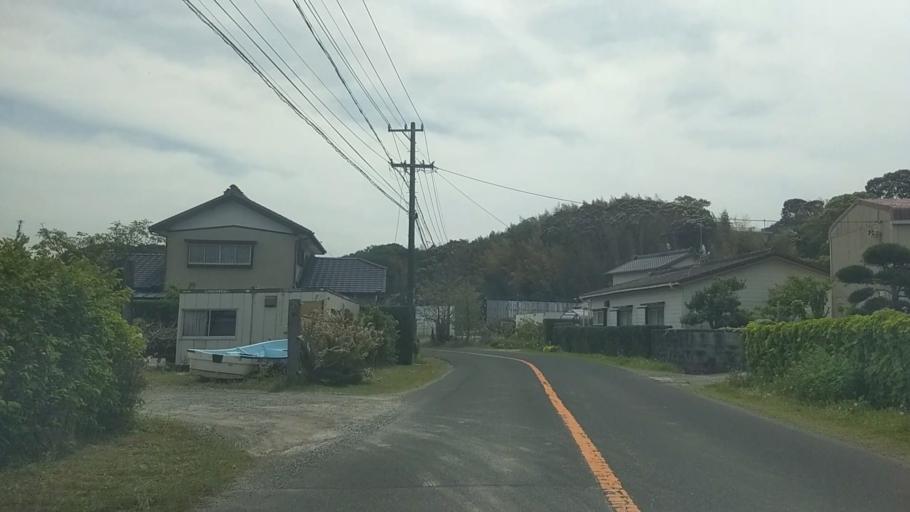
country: JP
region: Shizuoka
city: Kosai-shi
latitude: 34.7546
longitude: 137.5129
